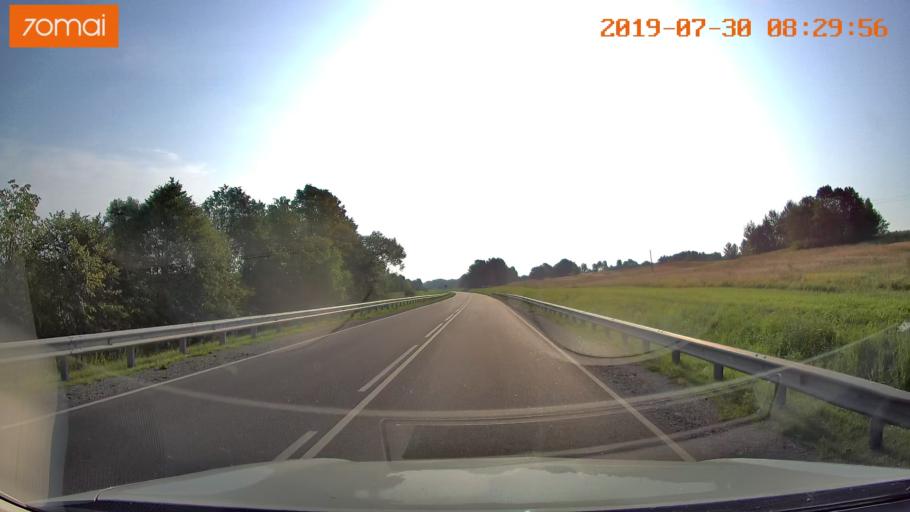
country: RU
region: Kaliningrad
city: Chernyakhovsk
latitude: 54.6327
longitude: 21.6737
